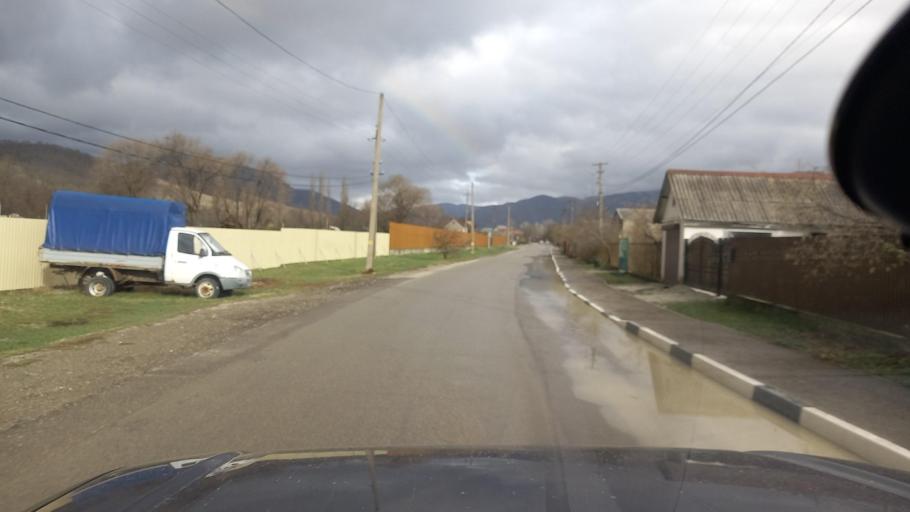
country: RU
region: Krasnodarskiy
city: Pshada
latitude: 44.4775
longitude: 38.3998
